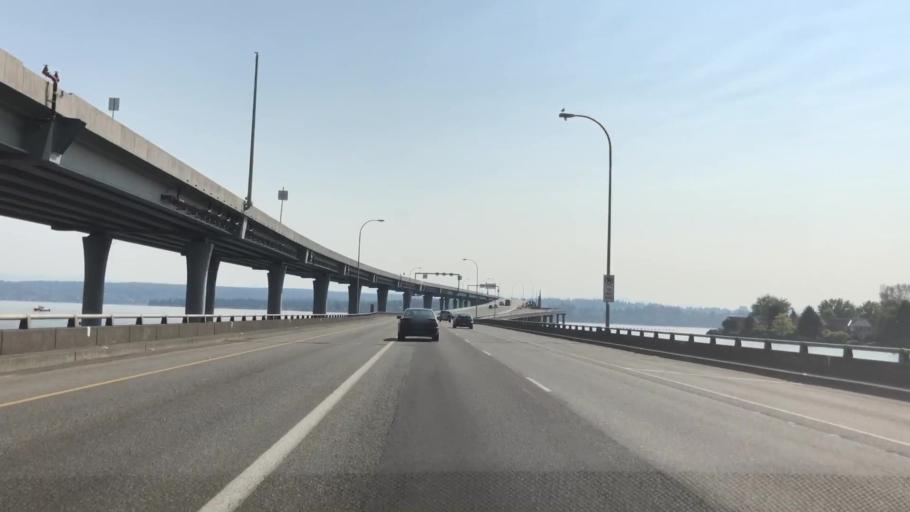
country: US
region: Washington
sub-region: King County
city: Medina
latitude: 47.6439
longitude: -122.2835
